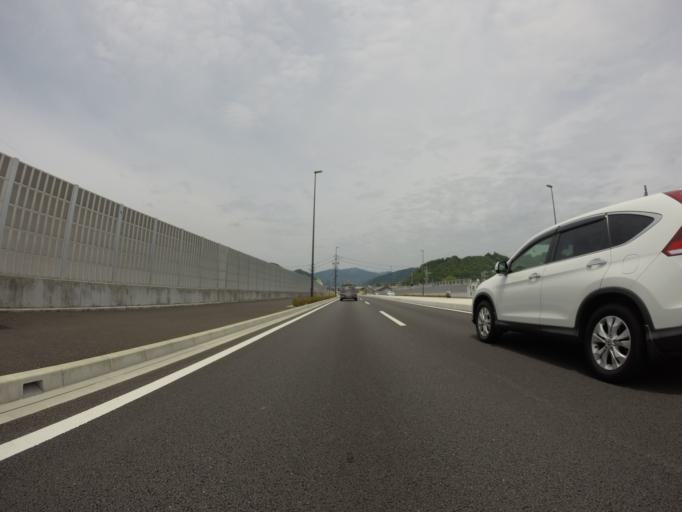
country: JP
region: Shizuoka
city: Shizuoka-shi
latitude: 34.9767
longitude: 138.3555
